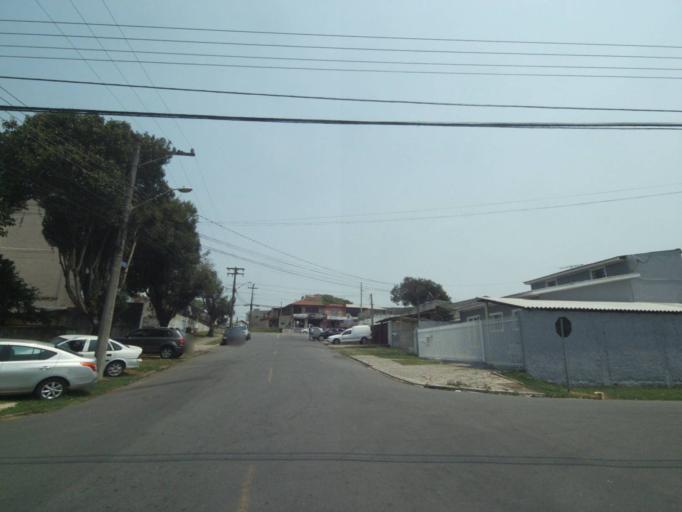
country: BR
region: Parana
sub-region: Sao Jose Dos Pinhais
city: Sao Jose dos Pinhais
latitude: -25.5284
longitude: -49.2481
